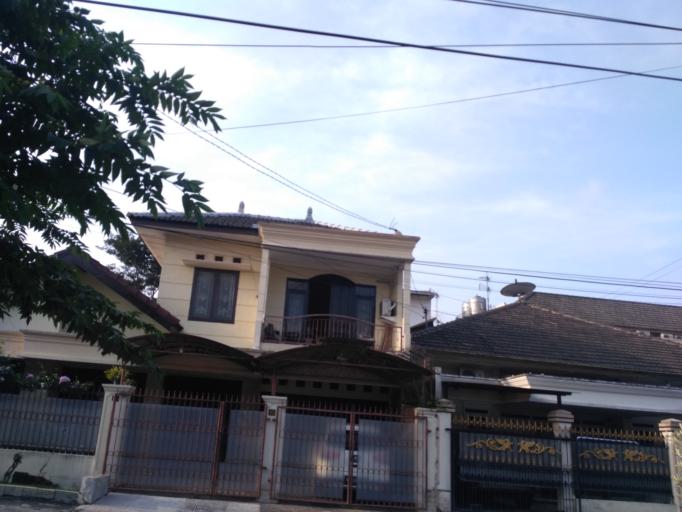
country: ID
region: East Java
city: Malang
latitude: -7.9370
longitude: 112.6367
